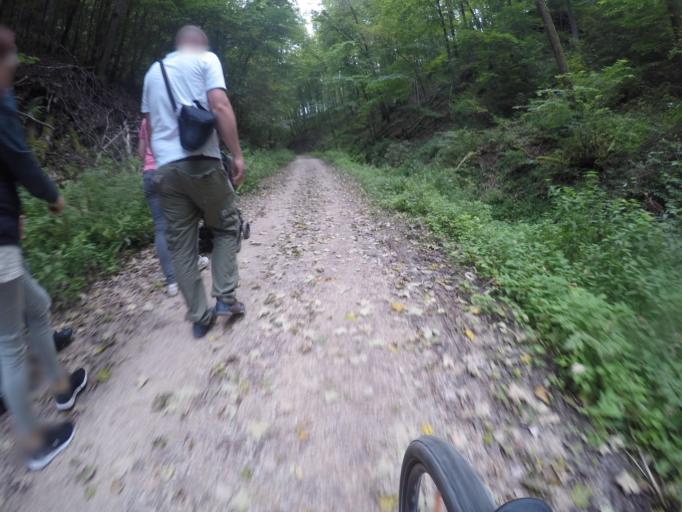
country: DE
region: Baden-Wuerttemberg
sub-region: Tuebingen Region
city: Munsingen
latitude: 48.4362
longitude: 9.4779
